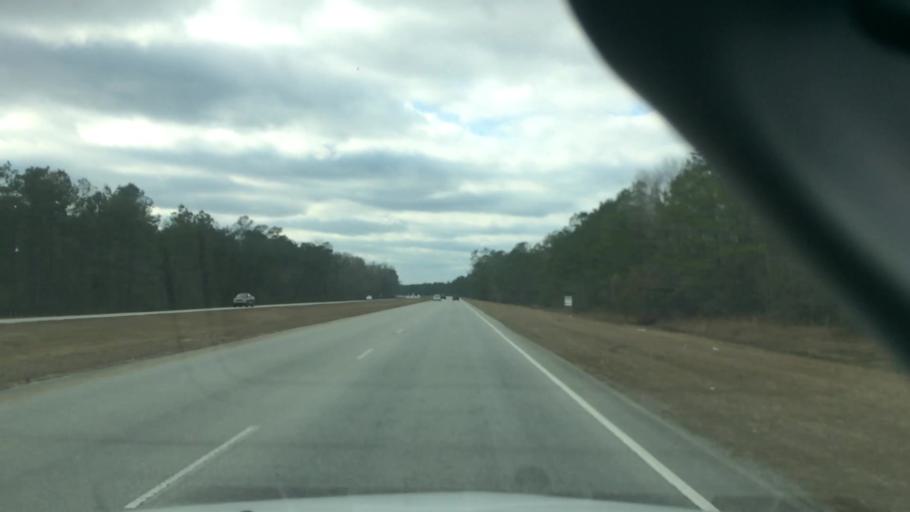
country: US
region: North Carolina
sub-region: Brunswick County
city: Bolivia
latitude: 34.0771
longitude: -78.1496
